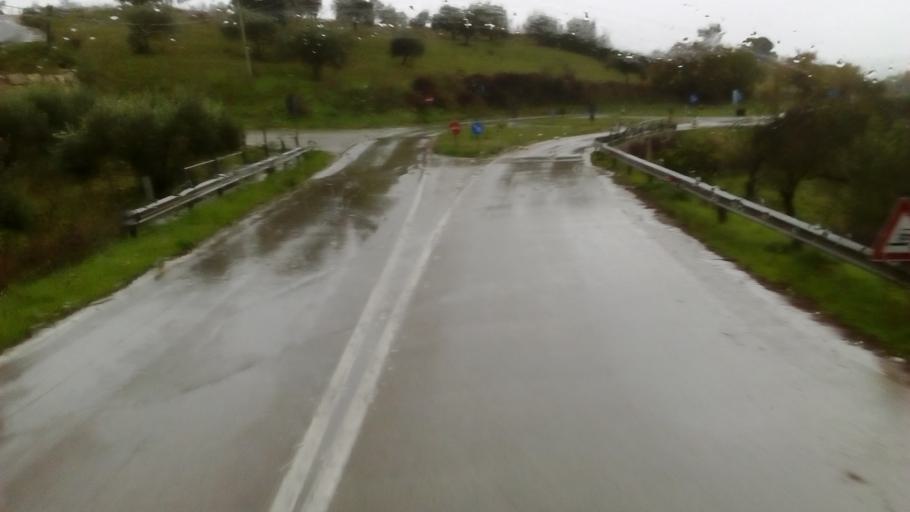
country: IT
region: Sicily
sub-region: Enna
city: Pietraperzia
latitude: 37.4296
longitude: 14.1690
